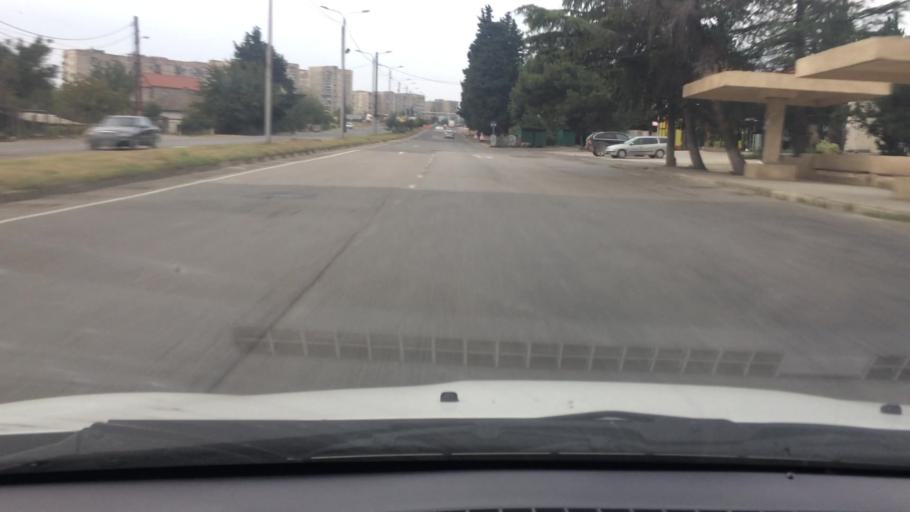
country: GE
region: T'bilisi
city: Tbilisi
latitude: 41.6491
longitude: 44.9021
